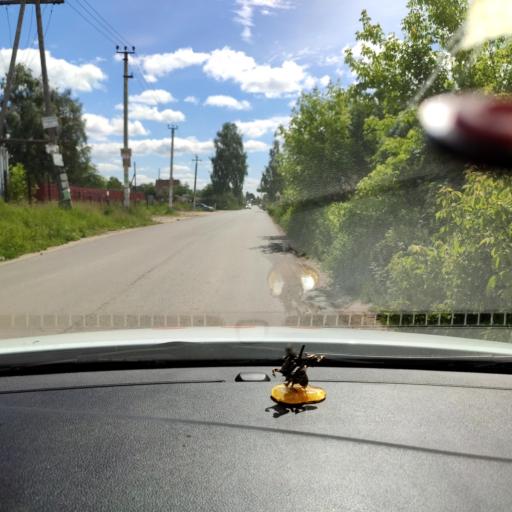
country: RU
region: Tatarstan
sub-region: Zelenodol'skiy Rayon
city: Vasil'yevo
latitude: 55.8312
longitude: 48.7300
